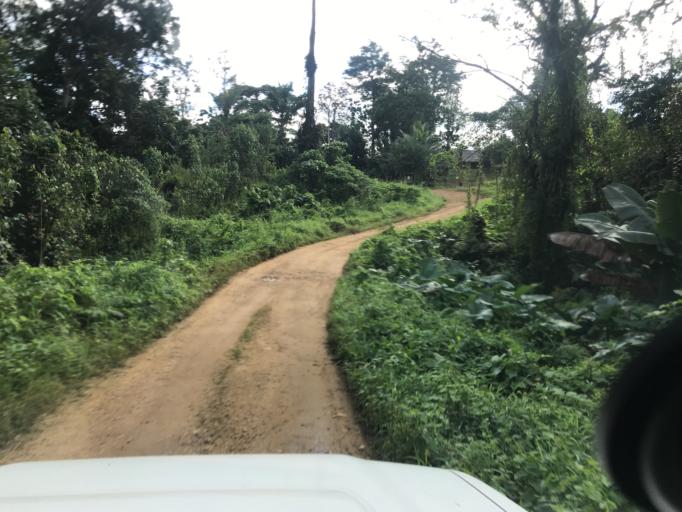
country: VU
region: Sanma
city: Luganville
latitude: -15.4623
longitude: 167.0744
